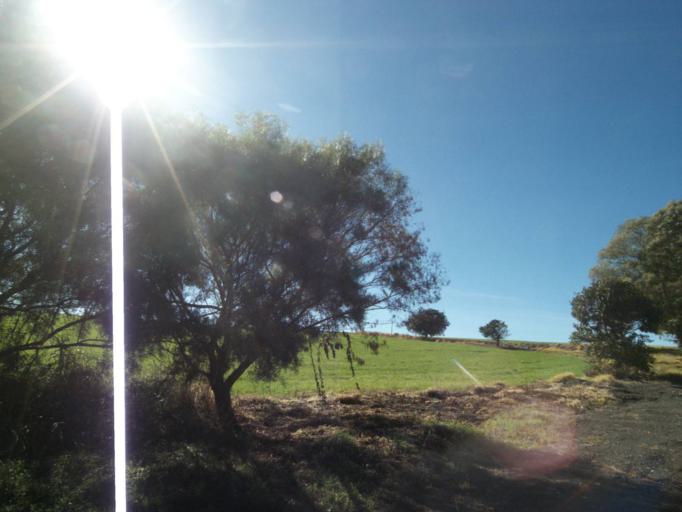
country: BR
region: Parana
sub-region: Tibagi
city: Tibagi
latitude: -24.5488
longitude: -50.2996
